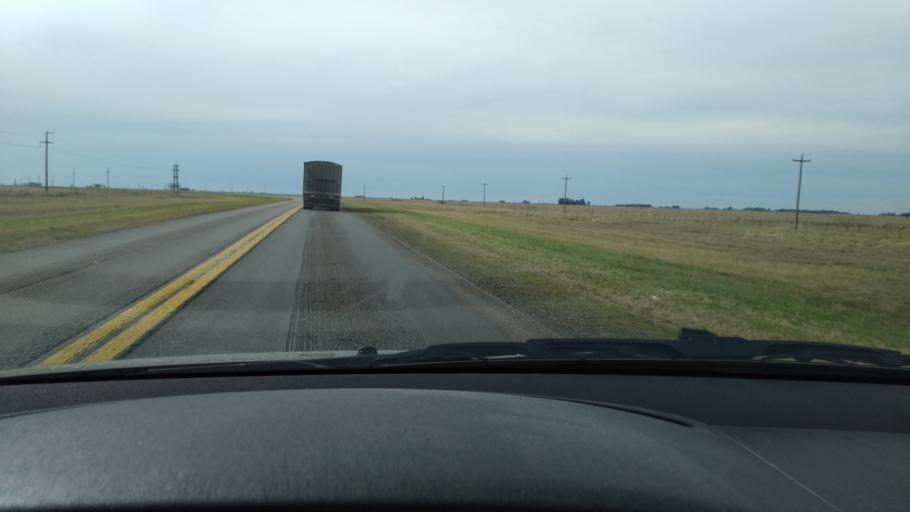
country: AR
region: Buenos Aires
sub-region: Partido de Azul
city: Azul
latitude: -36.7185
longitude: -59.7651
